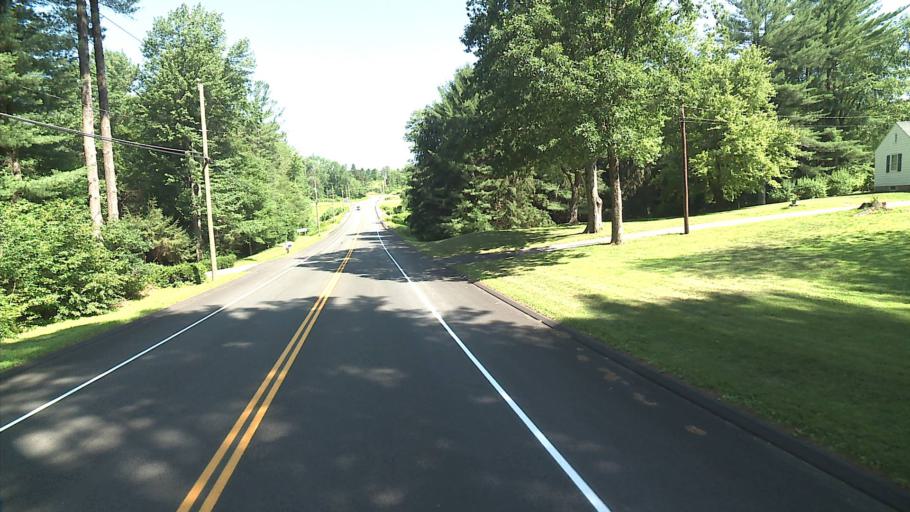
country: US
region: Connecticut
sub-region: Litchfield County
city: Northwest Harwinton
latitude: 41.7726
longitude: -73.0267
